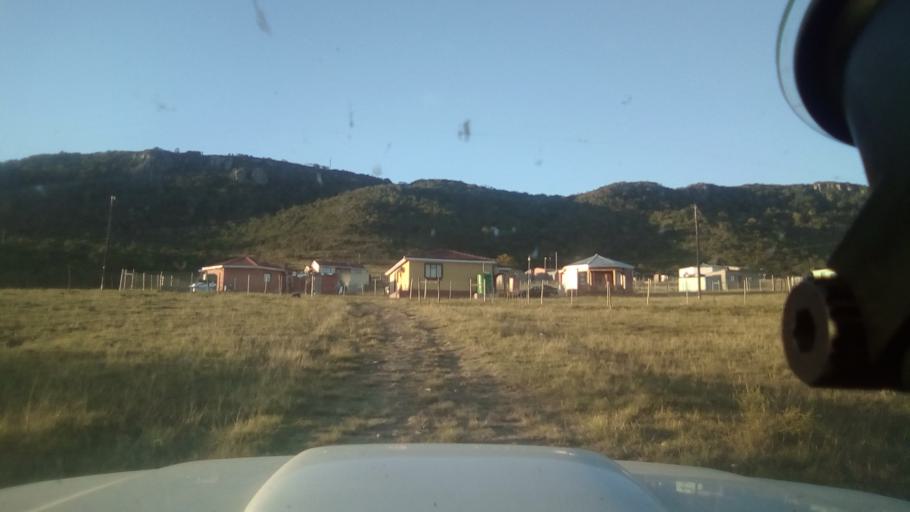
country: ZA
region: Eastern Cape
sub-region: Buffalo City Metropolitan Municipality
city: Bhisho
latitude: -32.7346
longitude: 27.3769
